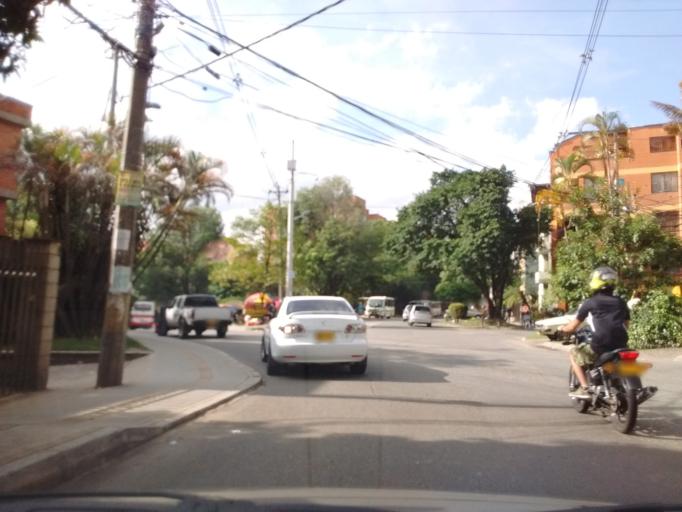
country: CO
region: Antioquia
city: Itagui
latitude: 6.2304
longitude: -75.6055
